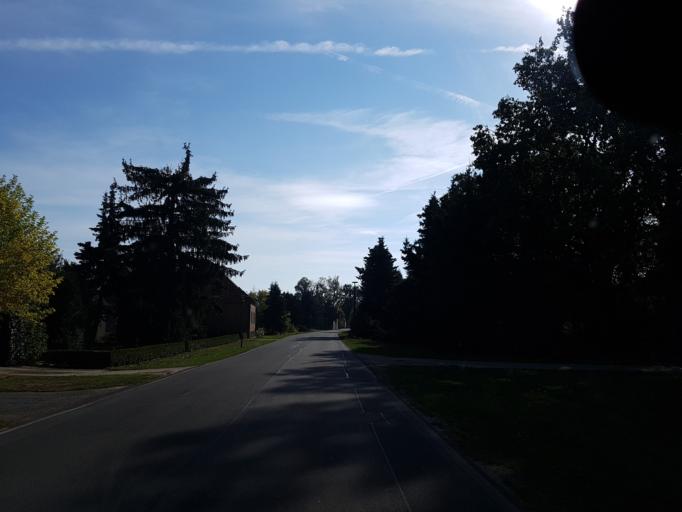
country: DE
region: Brandenburg
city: Doberlug-Kirchhain
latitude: 51.6770
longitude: 13.5091
